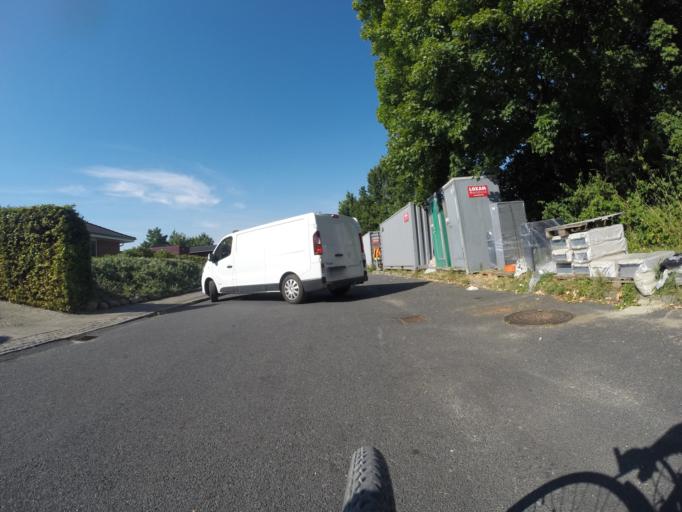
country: DK
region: Capital Region
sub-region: Herlev Kommune
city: Herlev
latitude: 55.7463
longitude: 12.4274
